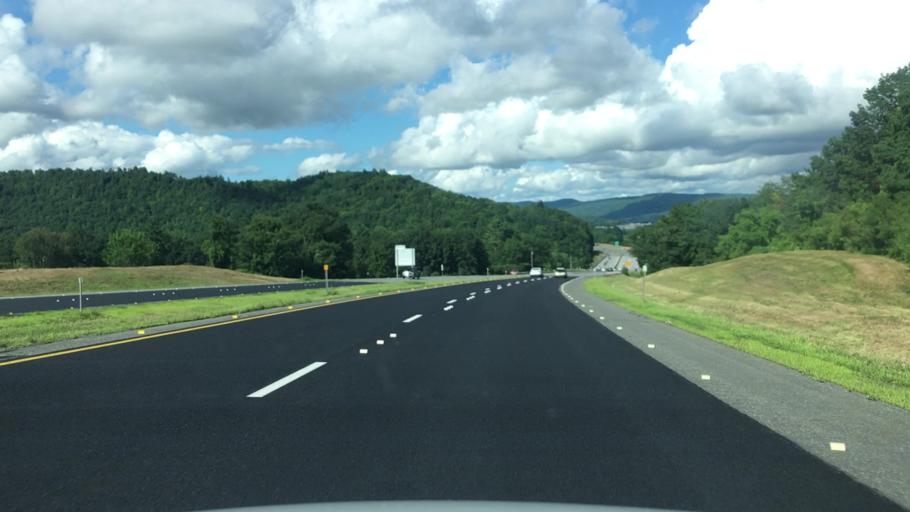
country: US
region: Vermont
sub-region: Windham County
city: Brattleboro
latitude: 42.8692
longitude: -72.5769
